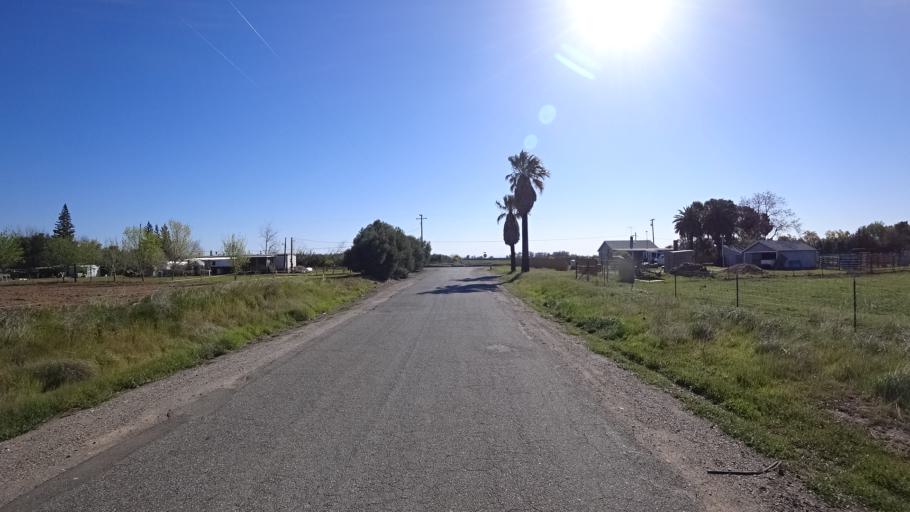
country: US
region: California
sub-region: Glenn County
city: Orland
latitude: 39.7368
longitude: -122.2168
